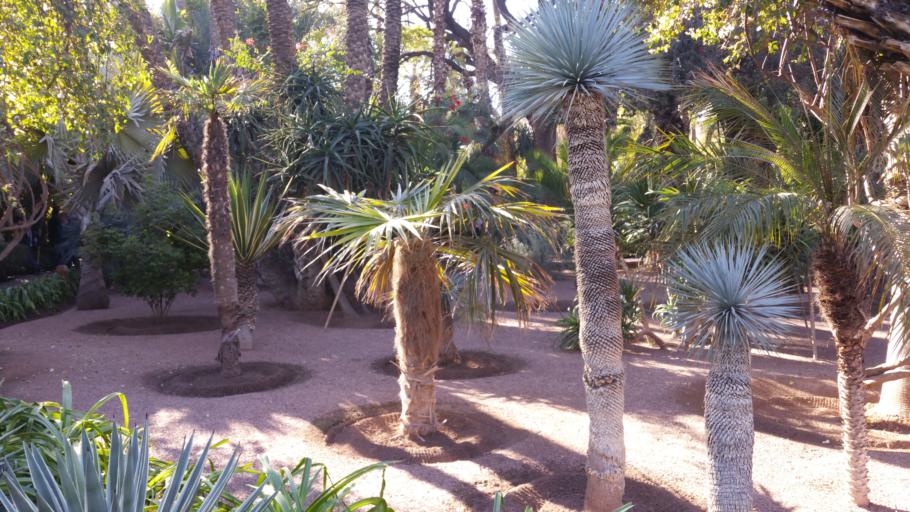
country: MA
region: Marrakech-Tensift-Al Haouz
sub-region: Marrakech
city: Marrakesh
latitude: 31.6414
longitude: -8.0030
